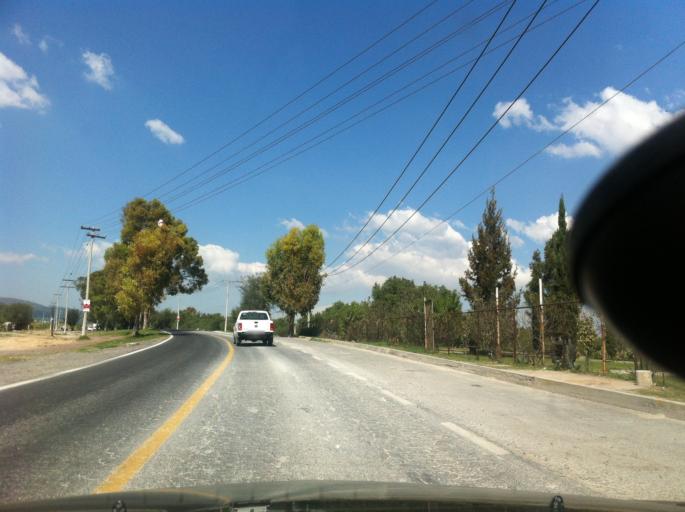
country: MX
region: Mexico
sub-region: Zumpango
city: Zumpango
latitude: 19.7747
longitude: -99.1193
